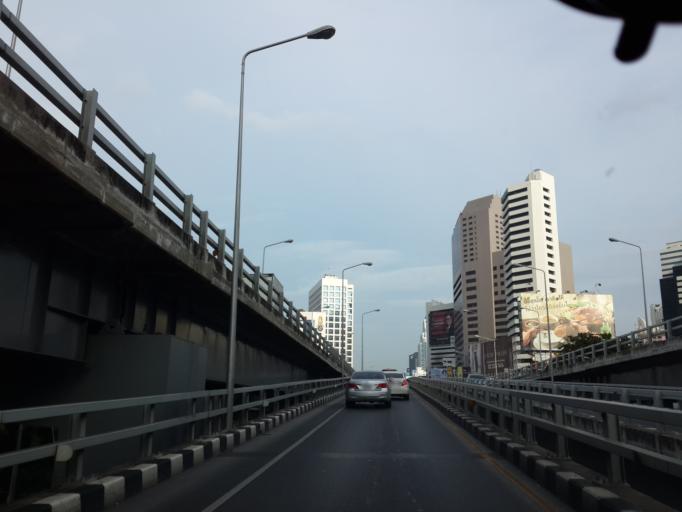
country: TH
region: Bangkok
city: Bang Rak
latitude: 13.7315
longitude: 100.5321
